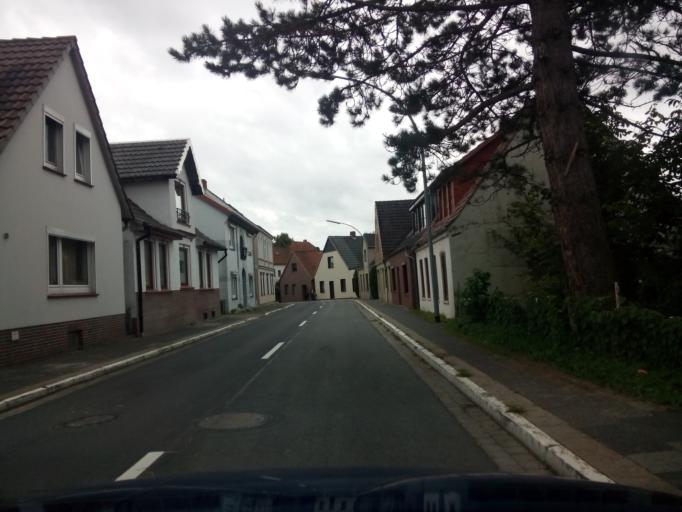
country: DE
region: Lower Saxony
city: Osterholz-Scharmbeck
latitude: 53.2351
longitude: 8.7848
